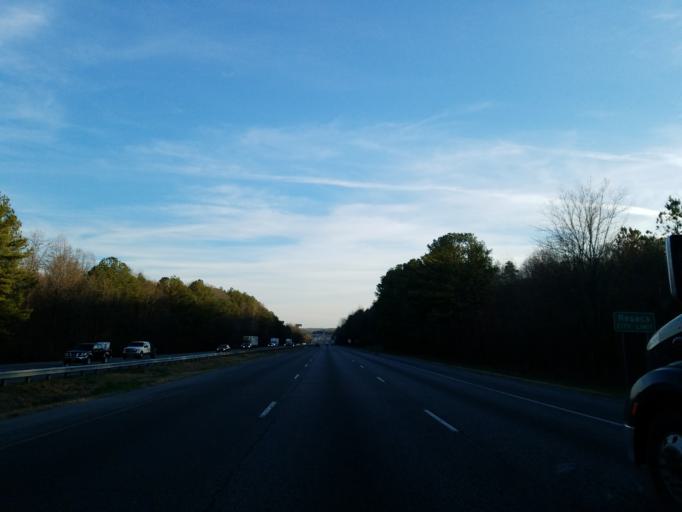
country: US
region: Georgia
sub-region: Gordon County
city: Calhoun
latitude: 34.5942
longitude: -84.9550
